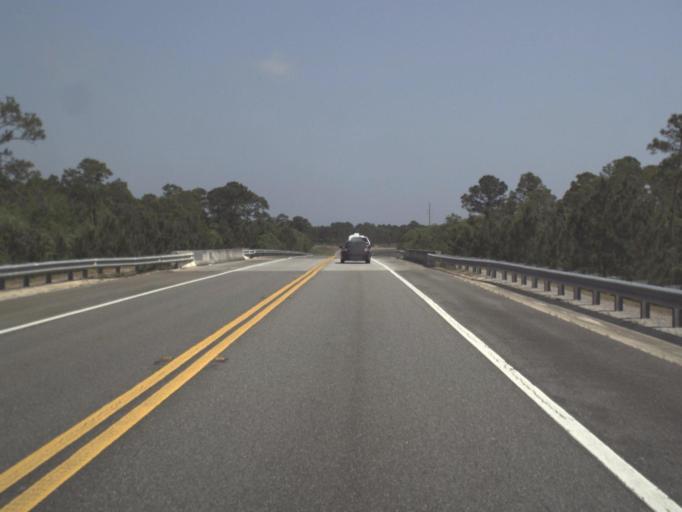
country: US
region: Florida
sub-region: Santa Rosa County
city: Tiger Point
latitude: 30.3975
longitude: -87.0739
